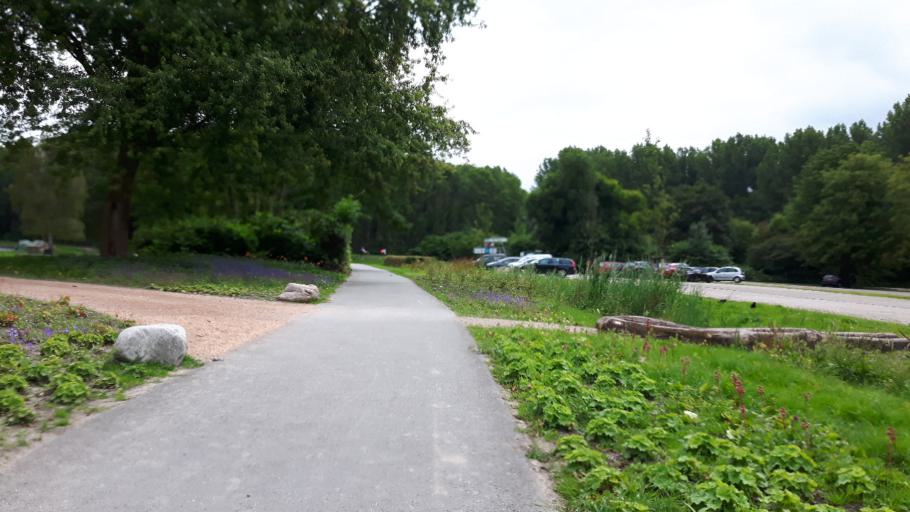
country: NL
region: South Holland
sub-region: Gemeente Lansingerland
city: Bergschenhoek
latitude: 51.9661
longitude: 4.5151
